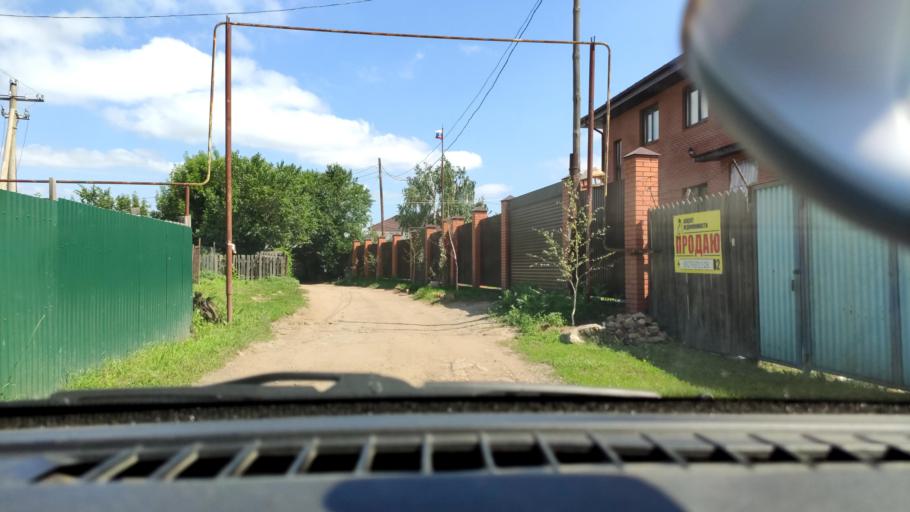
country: RU
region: Samara
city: Samara
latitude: 53.1289
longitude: 50.1781
